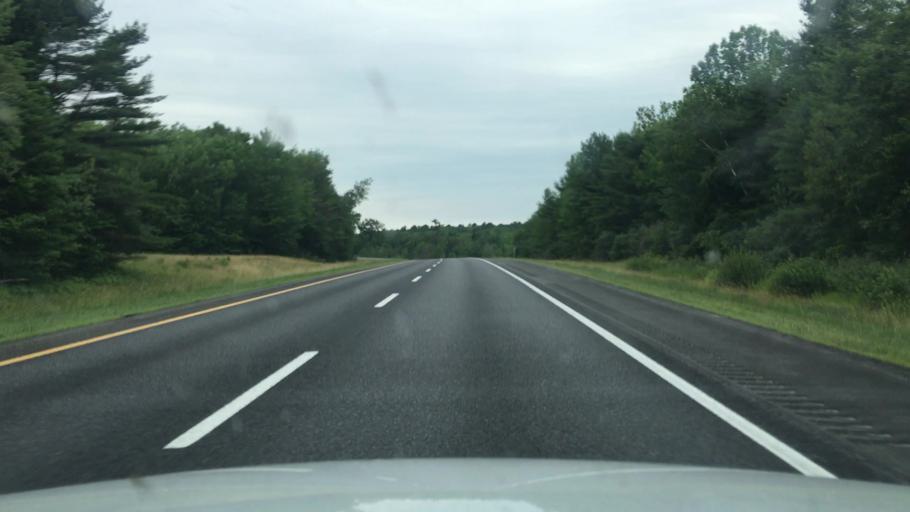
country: US
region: Maine
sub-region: Sagadahoc County
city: Topsham
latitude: 44.0287
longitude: -69.9141
